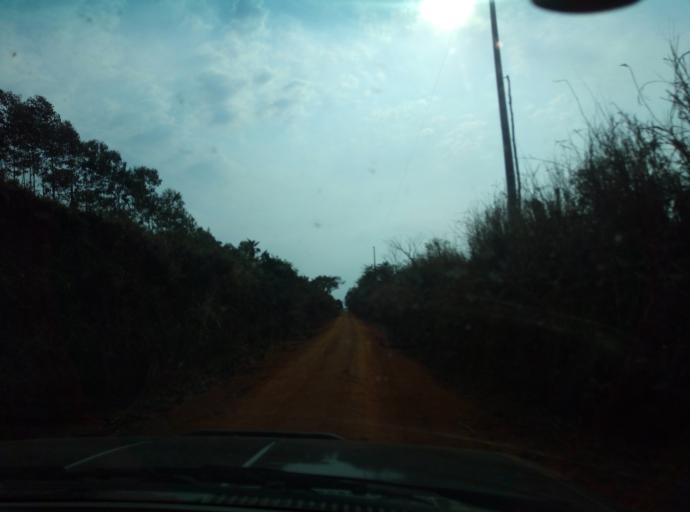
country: PY
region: Caaguazu
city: San Joaquin
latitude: -25.1481
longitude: -56.0998
